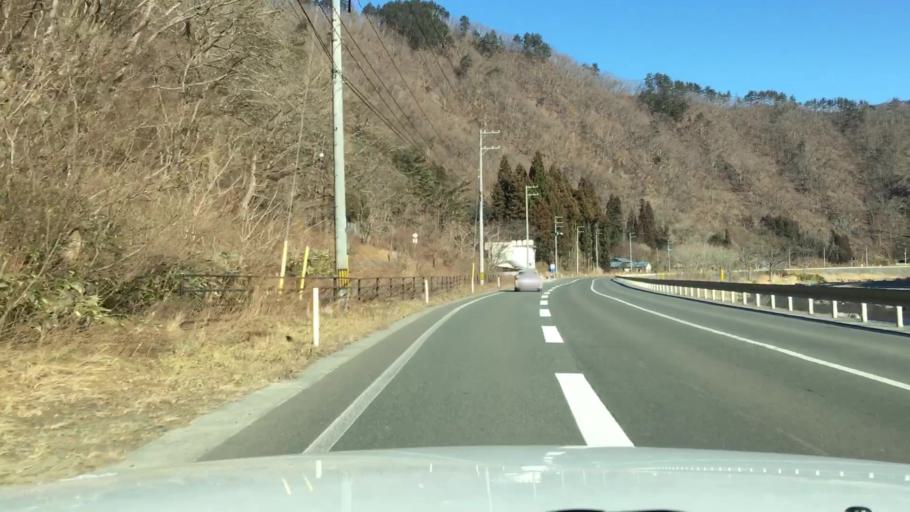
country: JP
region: Iwate
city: Miyako
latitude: 39.6134
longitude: 141.7882
